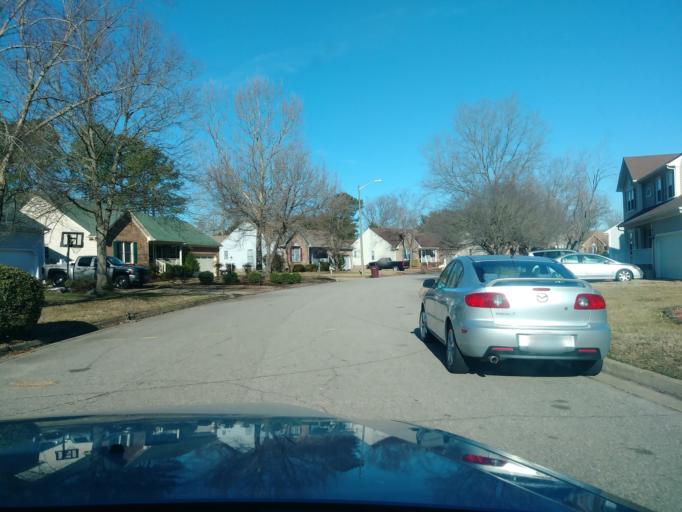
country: US
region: Virginia
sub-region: City of Chesapeake
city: Chesapeake
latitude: 36.7538
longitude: -76.2122
